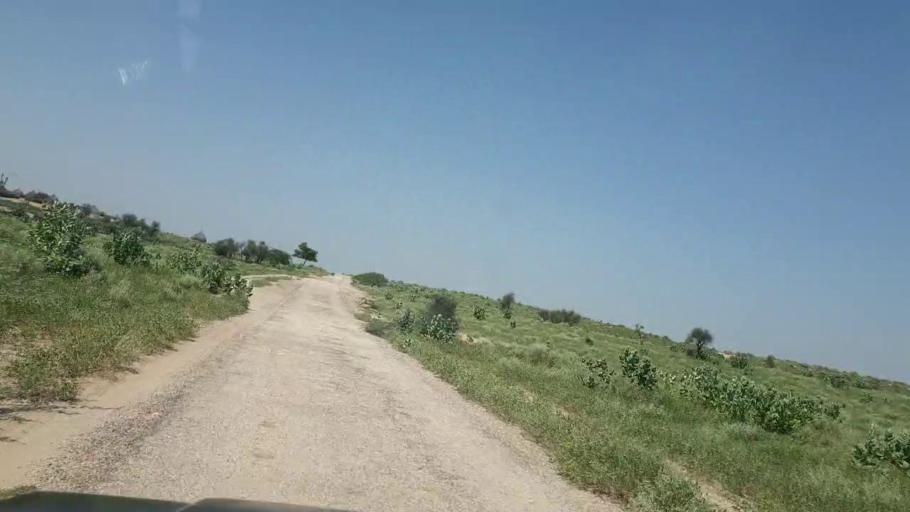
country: PK
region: Sindh
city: Chor
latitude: 25.3568
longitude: 70.3326
